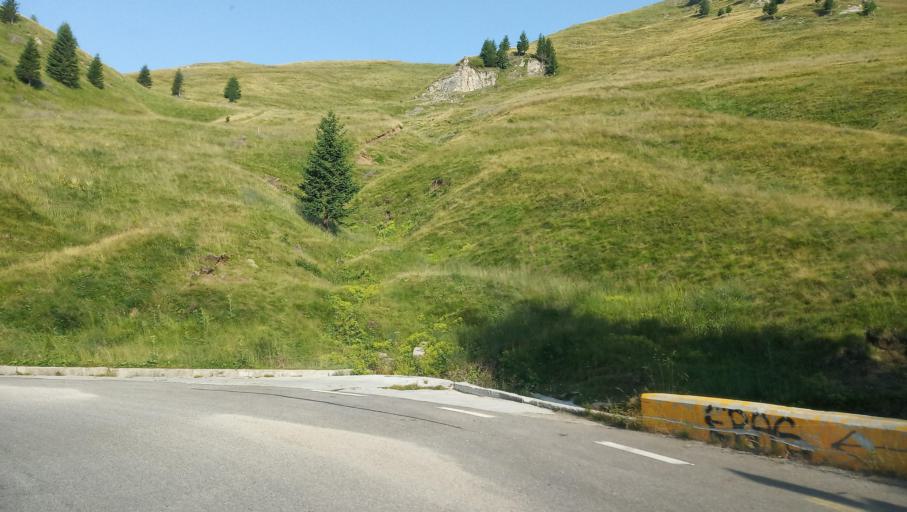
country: RO
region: Prahova
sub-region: Oras Sinaia
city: Sinaia
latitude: 45.3236
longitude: 25.4751
